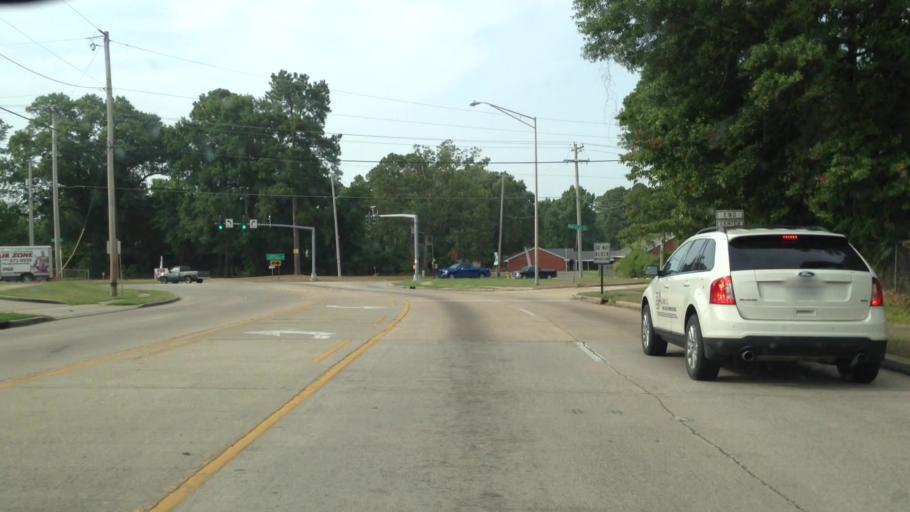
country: US
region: Louisiana
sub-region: De Soto Parish
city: Stonewall
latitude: 32.3954
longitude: -93.8147
